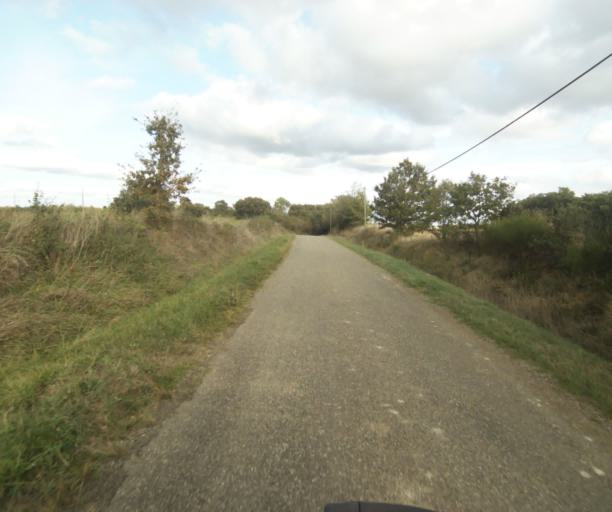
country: FR
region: Midi-Pyrenees
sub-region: Departement de la Haute-Garonne
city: Launac
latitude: 43.8246
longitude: 1.1103
